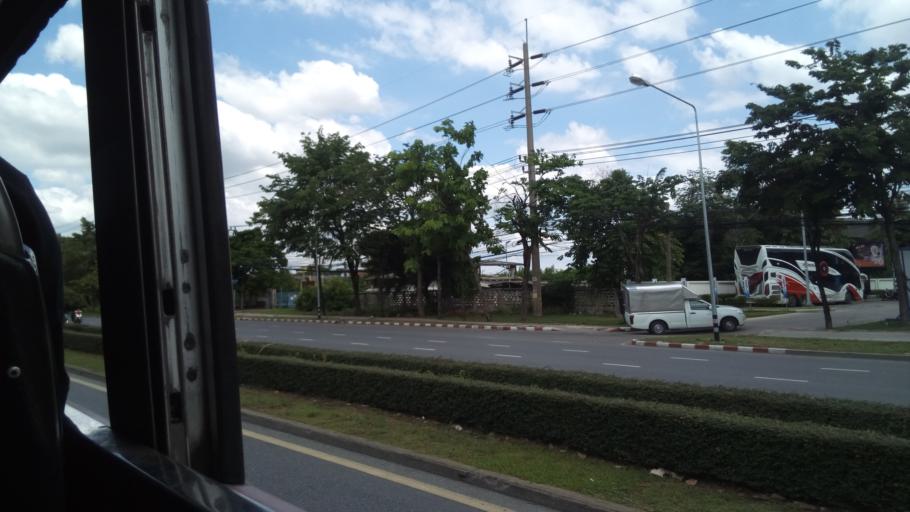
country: TH
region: Bangkok
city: Sai Mai
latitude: 13.9415
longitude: 100.6241
